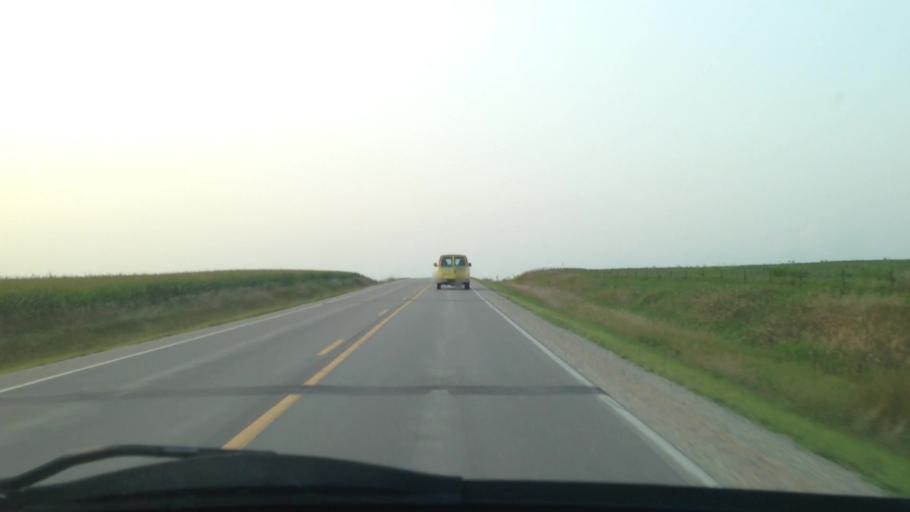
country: US
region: Iowa
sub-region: Benton County
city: Atkins
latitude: 42.0293
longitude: -91.8741
